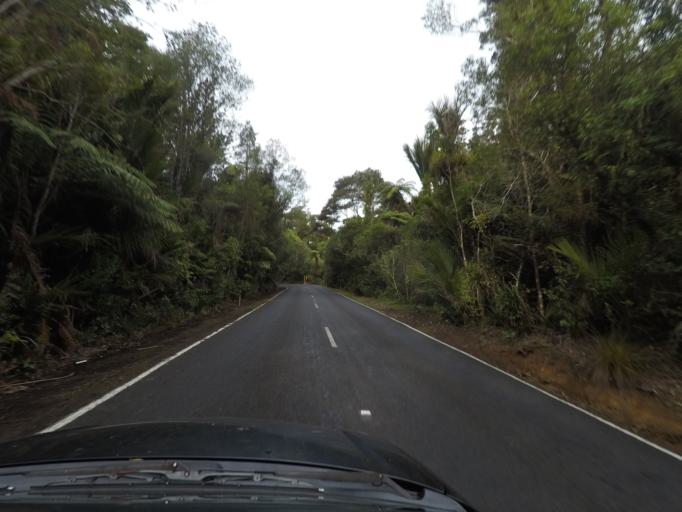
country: NZ
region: Auckland
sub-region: Auckland
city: Titirangi
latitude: -36.9436
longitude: 174.5875
